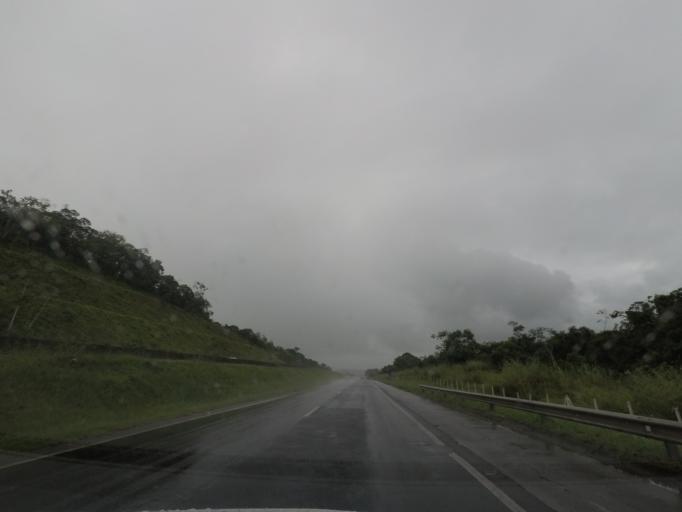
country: BR
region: Sao Paulo
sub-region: Registro
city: Registro
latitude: -24.4377
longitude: -47.7943
